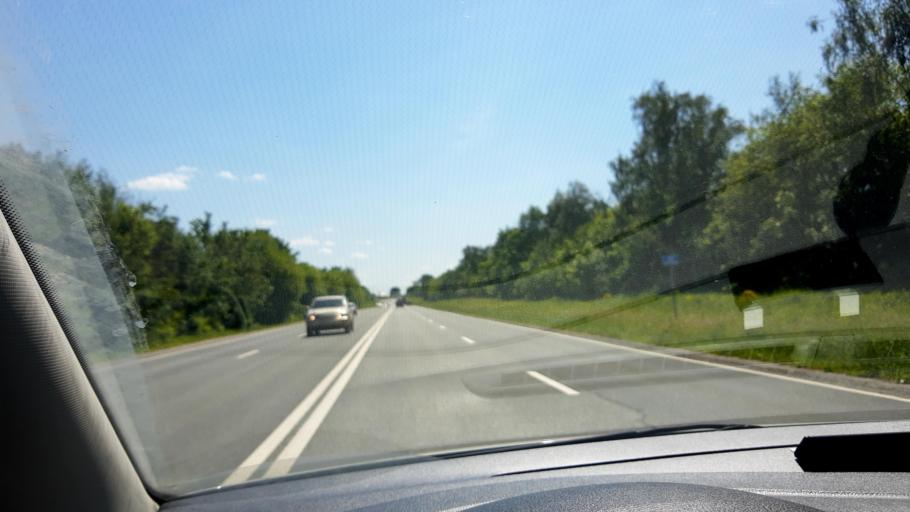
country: RU
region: Moskovskaya
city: Bronnitsy
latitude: 55.4515
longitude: 38.2058
